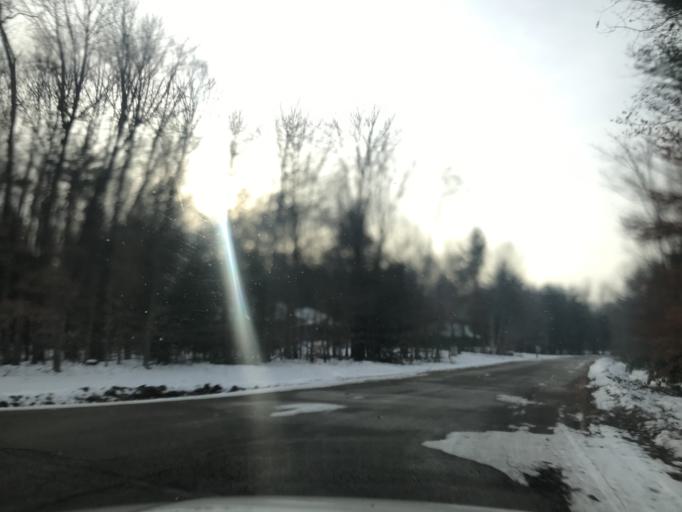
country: US
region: Wisconsin
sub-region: Brown County
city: Suamico
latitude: 44.6915
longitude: -88.0615
